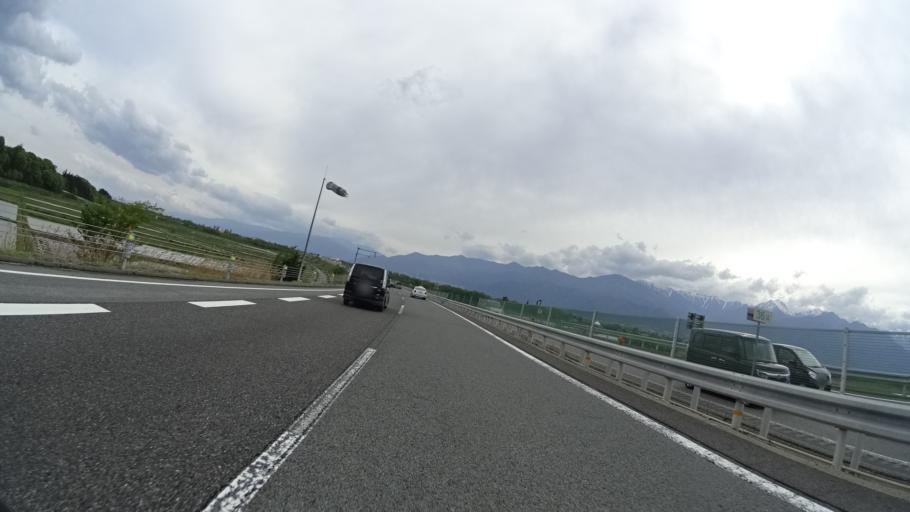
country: JP
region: Nagano
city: Toyoshina
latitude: 36.3272
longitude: 137.9257
